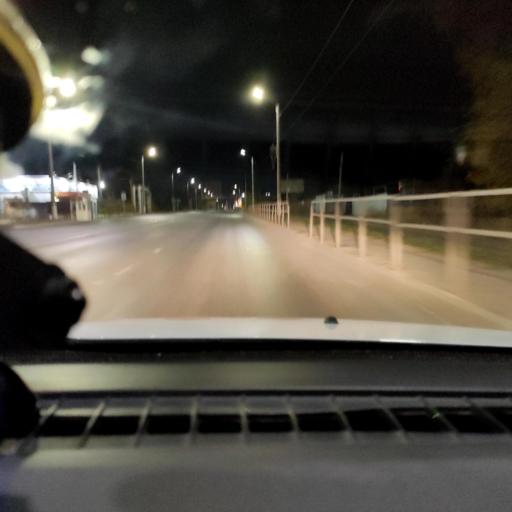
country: RU
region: Samara
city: Novokuybyshevsk
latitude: 53.0899
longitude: 49.9426
